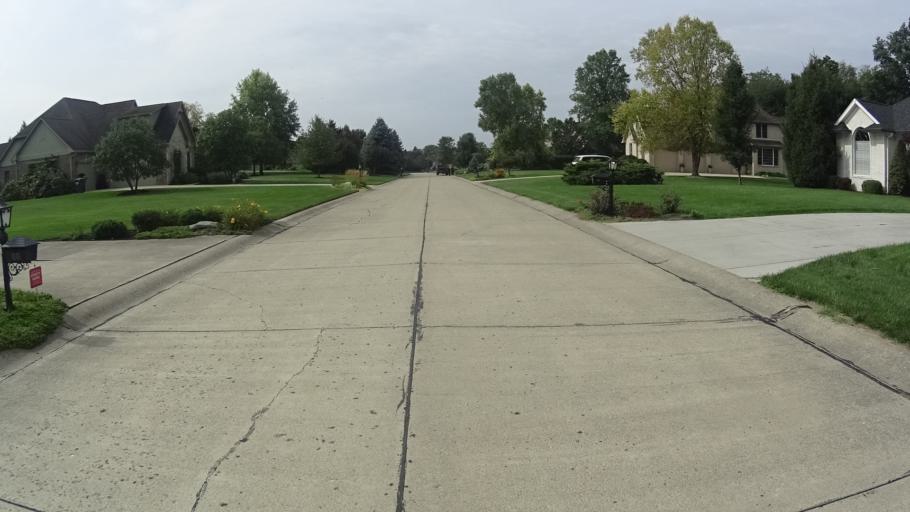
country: US
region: Indiana
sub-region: Madison County
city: Pendleton
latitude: 40.0148
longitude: -85.7884
